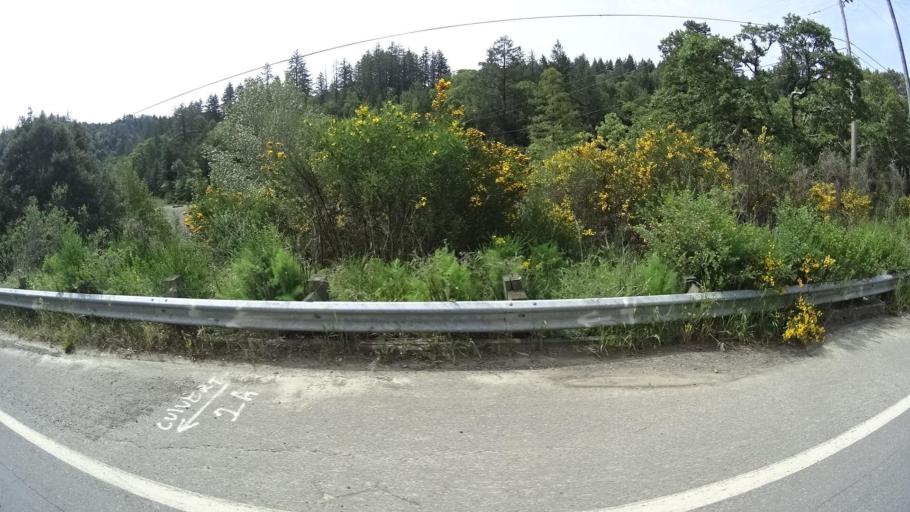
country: US
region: California
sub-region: Humboldt County
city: Redway
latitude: 40.1168
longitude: -123.8000
